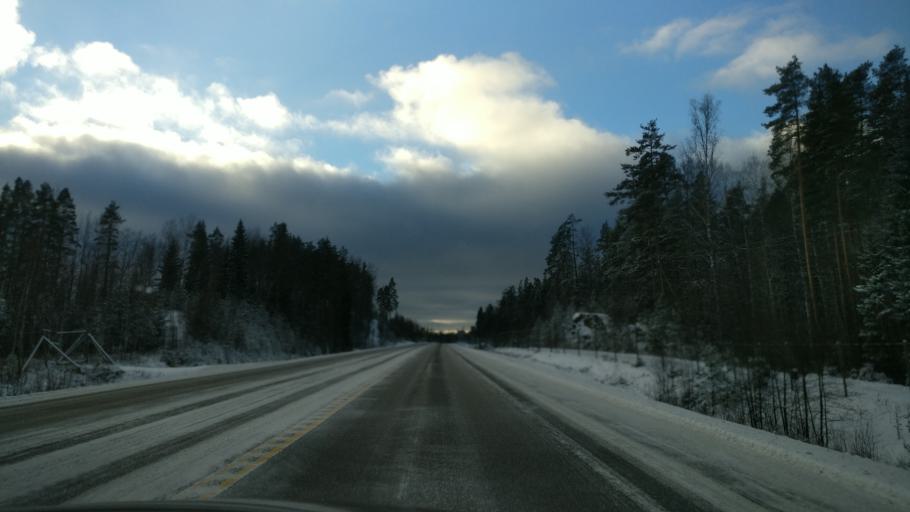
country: FI
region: Paijanne Tavastia
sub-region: Lahti
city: Heinola
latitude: 61.3403
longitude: 26.1883
